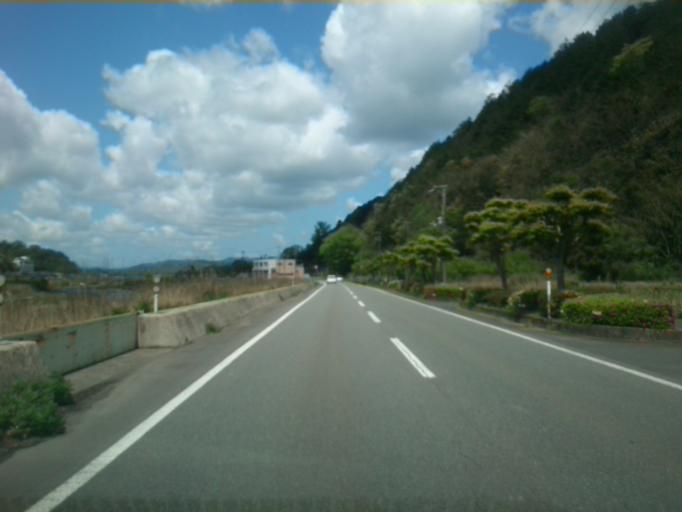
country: JP
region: Hyogo
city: Toyooka
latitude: 35.4529
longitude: 134.8719
